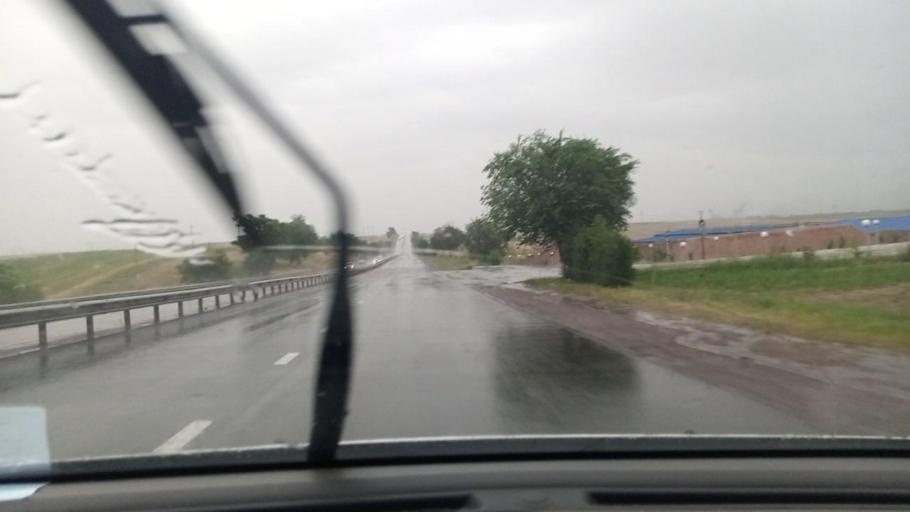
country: UZ
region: Toshkent
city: Ohangaron
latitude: 40.9569
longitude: 69.5628
